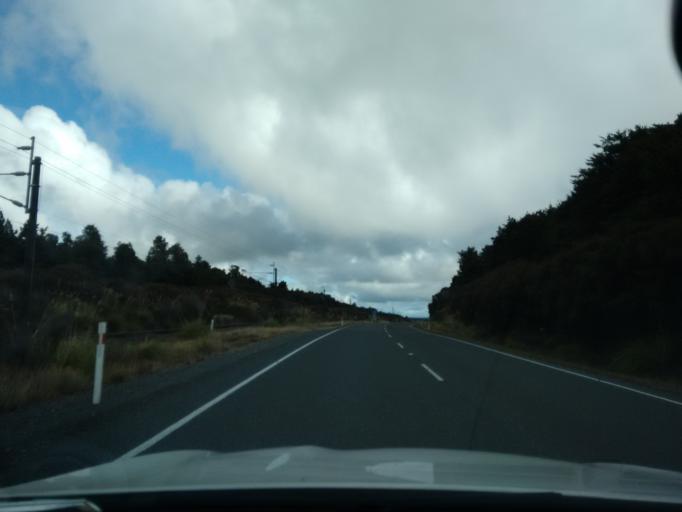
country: NZ
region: Manawatu-Wanganui
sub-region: Ruapehu District
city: Waiouru
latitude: -39.3077
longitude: 175.3898
